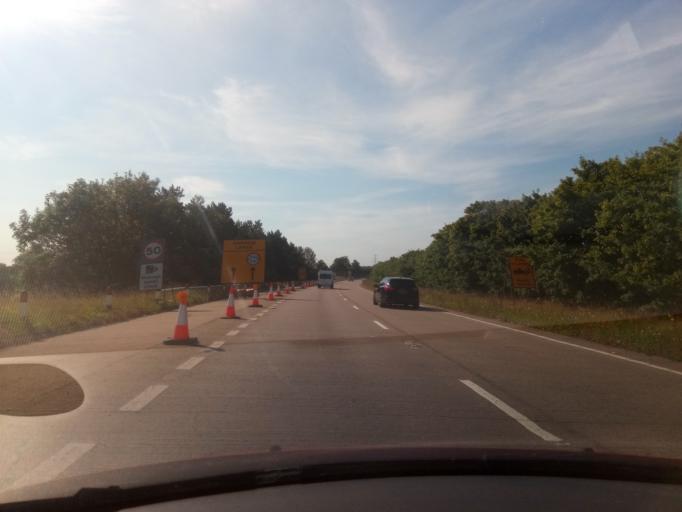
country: GB
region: England
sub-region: Stockton-on-Tees
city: Billingham
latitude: 54.6368
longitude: -1.3003
